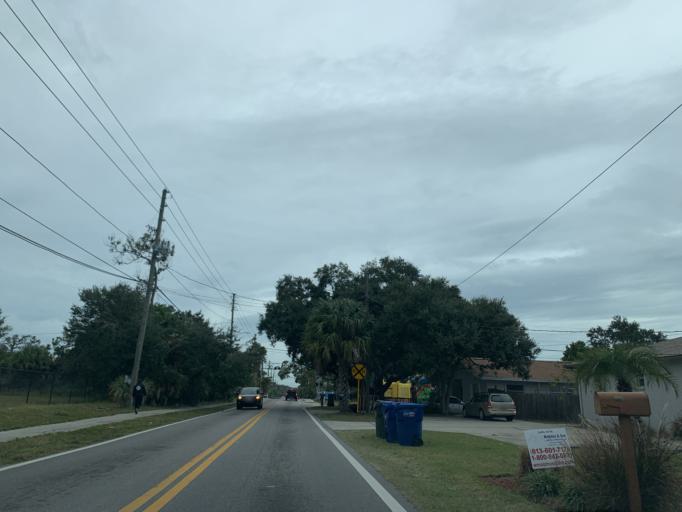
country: US
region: Florida
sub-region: Pinellas County
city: Belleair
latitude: 27.9352
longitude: -82.7929
